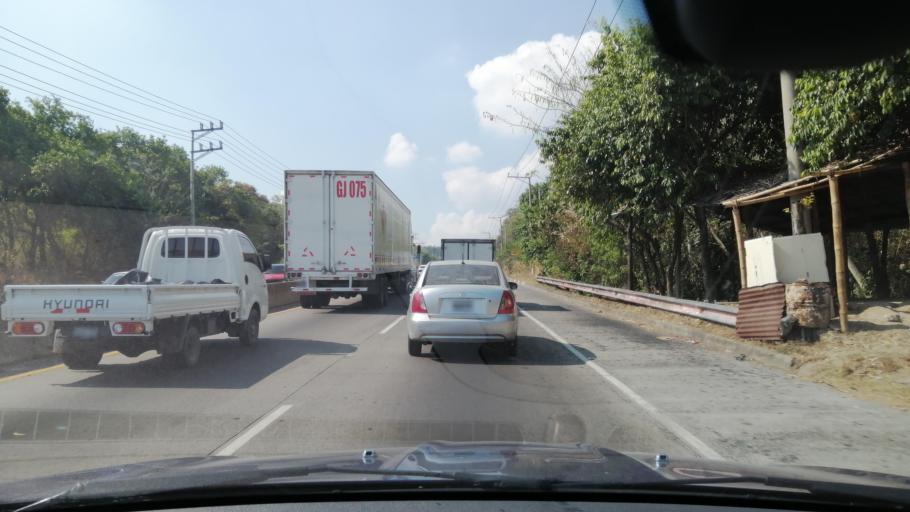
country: SV
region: San Salvador
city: Ayutuxtepeque
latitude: 13.7545
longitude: -89.2168
